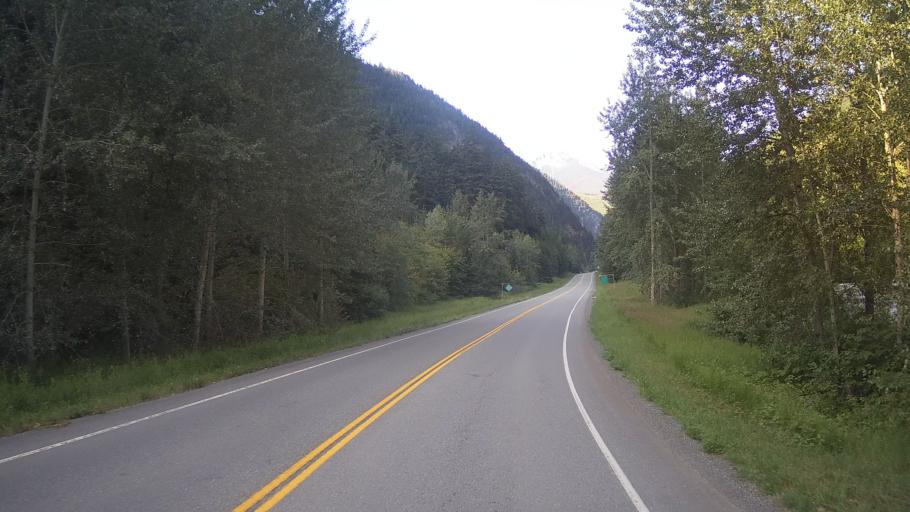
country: CA
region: British Columbia
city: Lillooet
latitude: 50.5612
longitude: -122.0915
